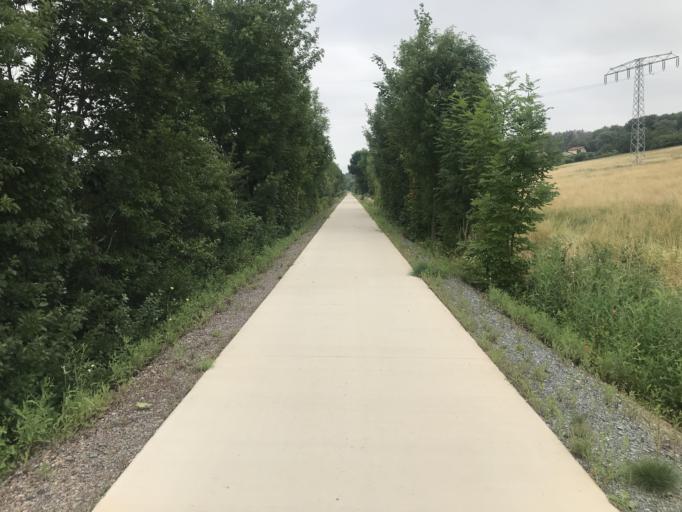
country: DE
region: Saxony-Anhalt
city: Rieder
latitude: 51.7307
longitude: 11.1580
